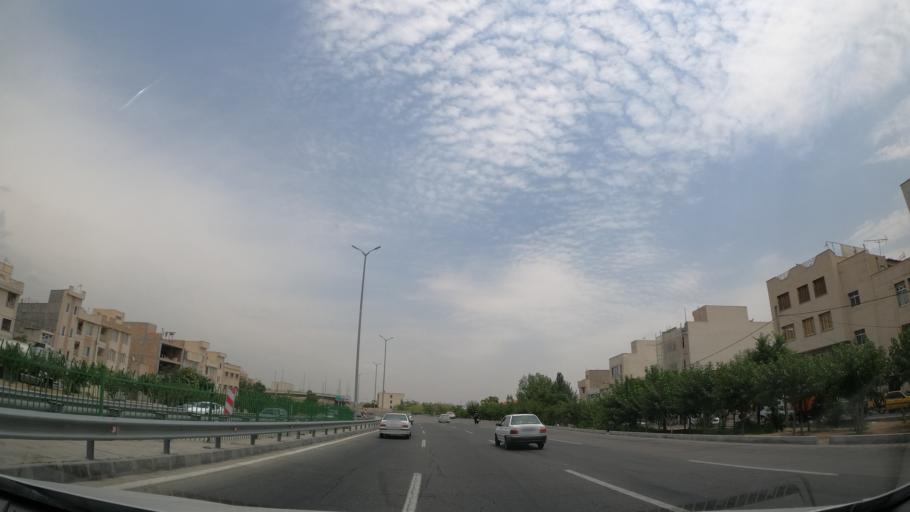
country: IR
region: Tehran
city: Shahr-e Qods
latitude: 35.7387
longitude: 51.2626
